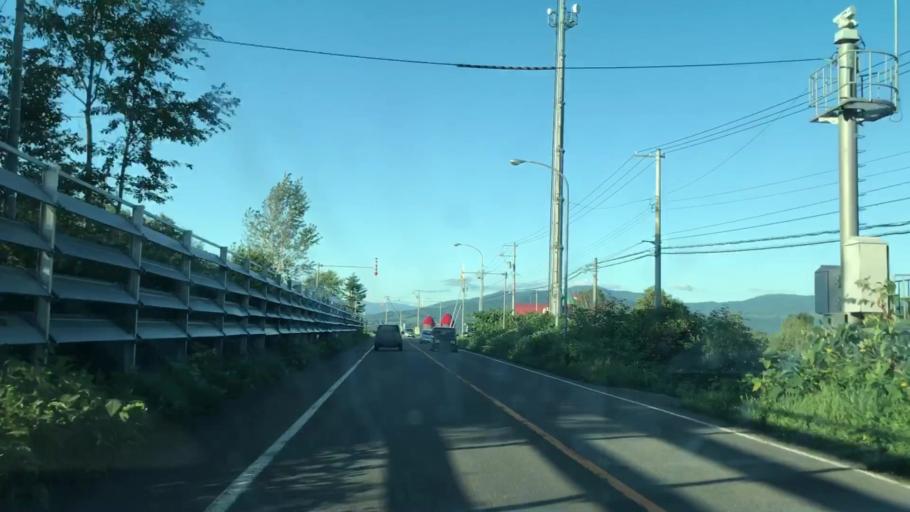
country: JP
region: Hokkaido
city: Date
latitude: 42.6249
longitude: 140.7975
